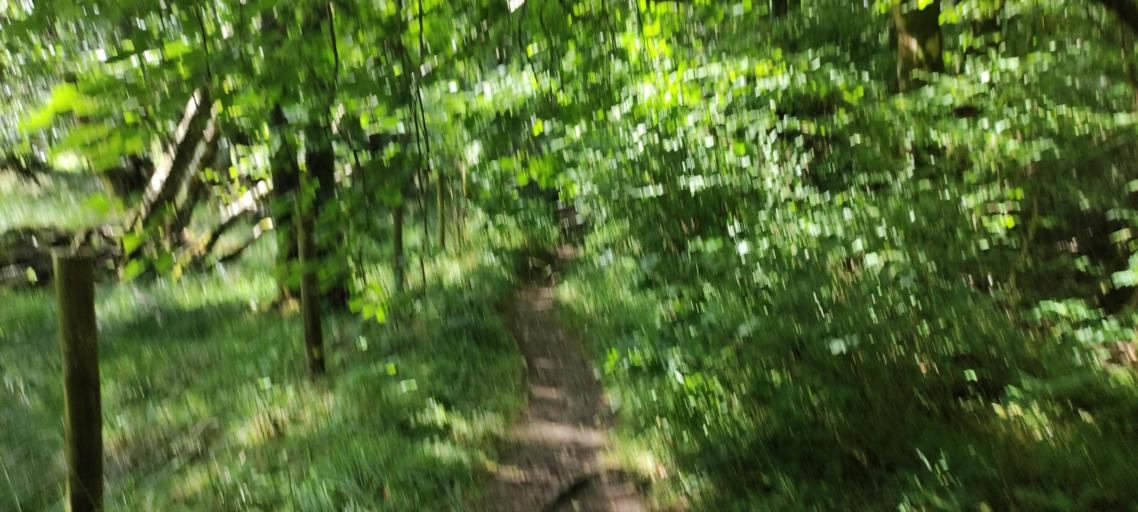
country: GB
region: England
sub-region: Cumbria
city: Cockermouth
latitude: 54.6639
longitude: -3.2408
